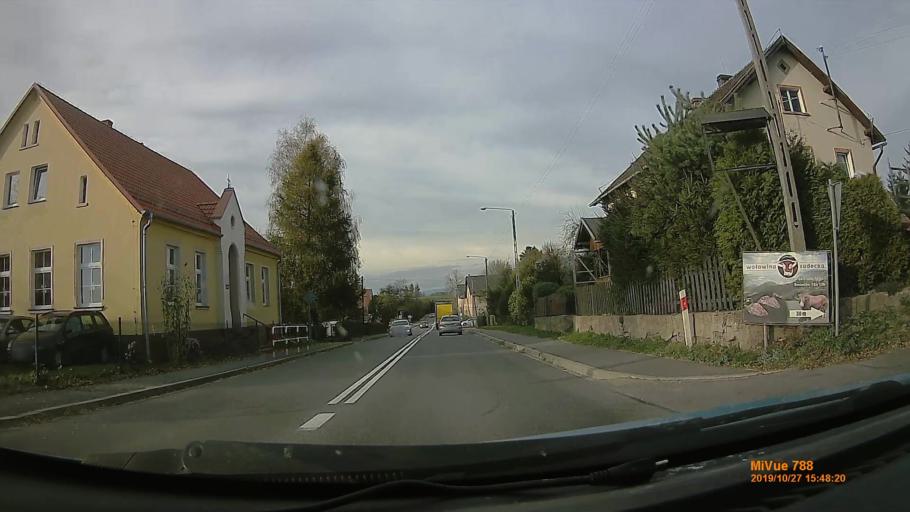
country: PL
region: Lower Silesian Voivodeship
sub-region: Powiat klodzki
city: Bozkow
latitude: 50.4966
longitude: 16.5866
